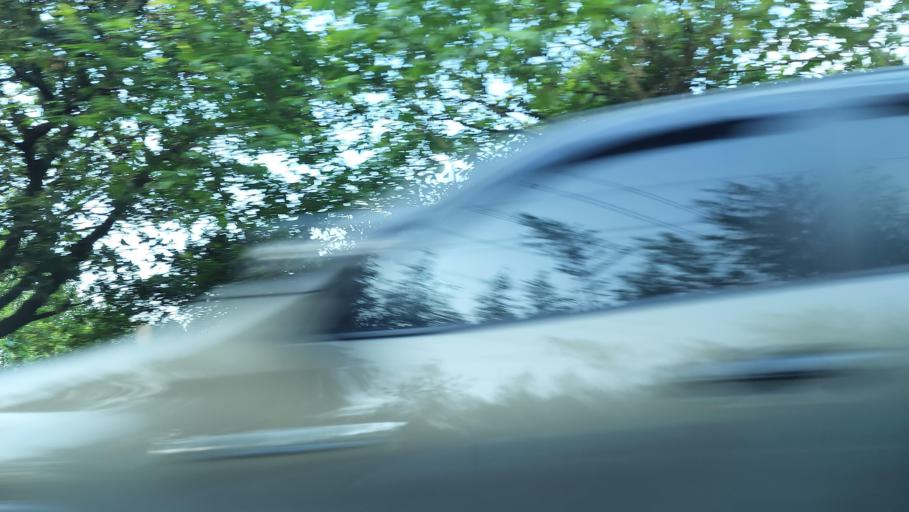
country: TW
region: Taiwan
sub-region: Keelung
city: Keelung
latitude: 25.1793
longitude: 121.6470
